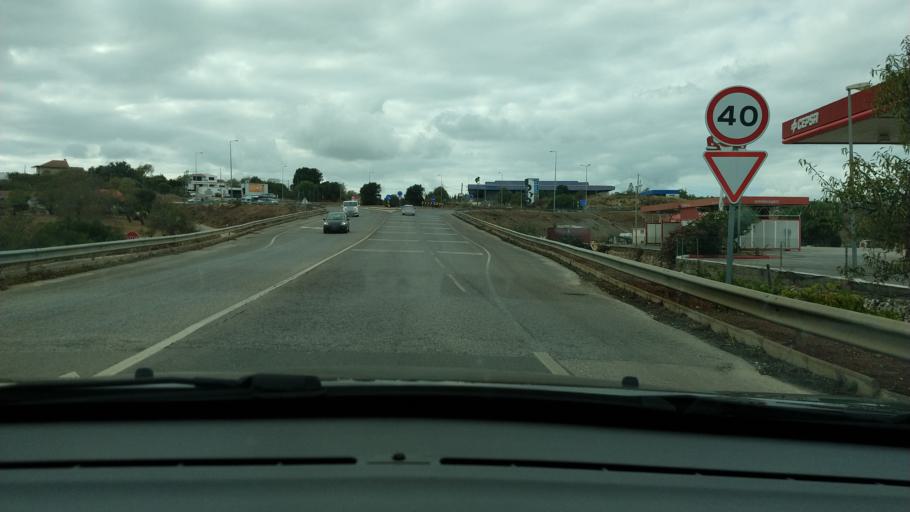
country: PT
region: Faro
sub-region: Lagos
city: Lagos
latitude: 37.1016
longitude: -8.6926
